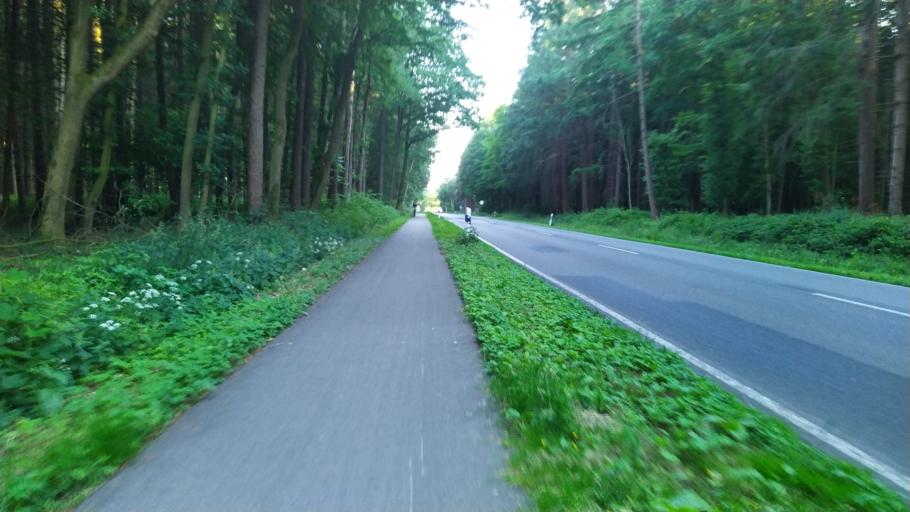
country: DE
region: Lower Saxony
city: Alfstedt
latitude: 53.5390
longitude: 9.0562
